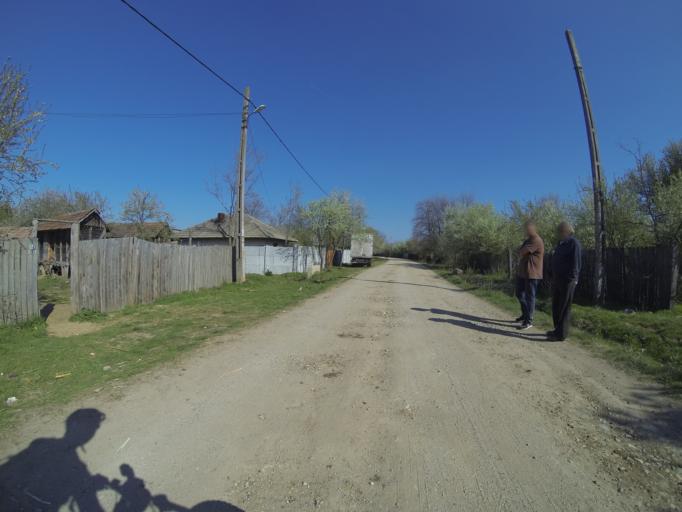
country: RO
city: Varvoru
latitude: 44.2253
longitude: 23.6219
